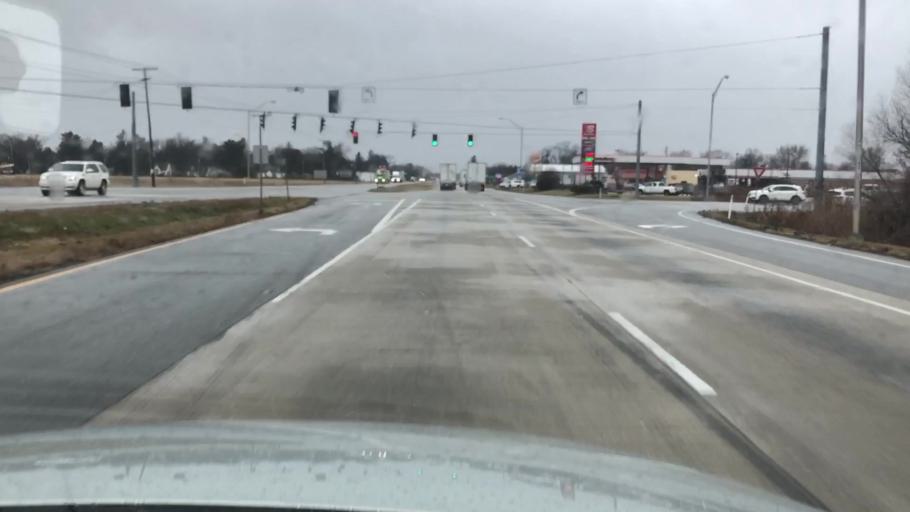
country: US
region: Indiana
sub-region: LaPorte County
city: Wanatah
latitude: 41.4341
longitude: -86.8905
